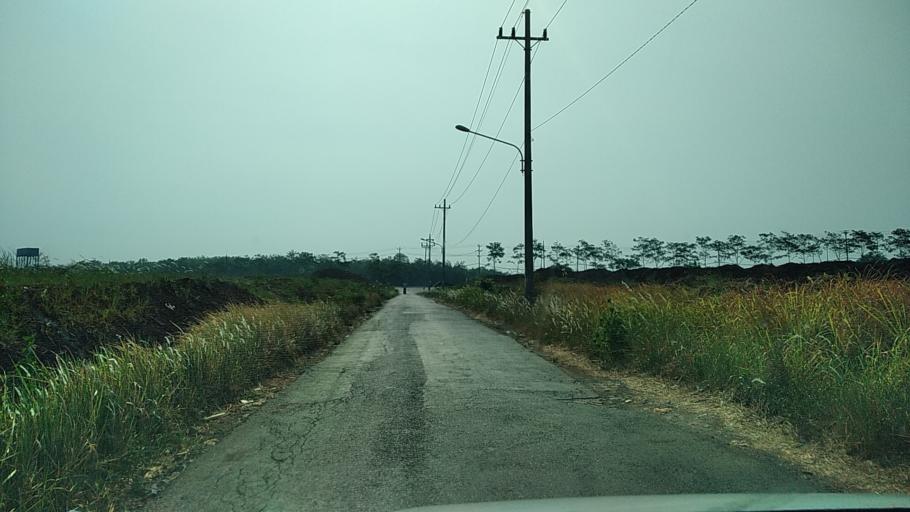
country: ID
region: Central Java
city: Semarang
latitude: -7.0411
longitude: 110.3319
